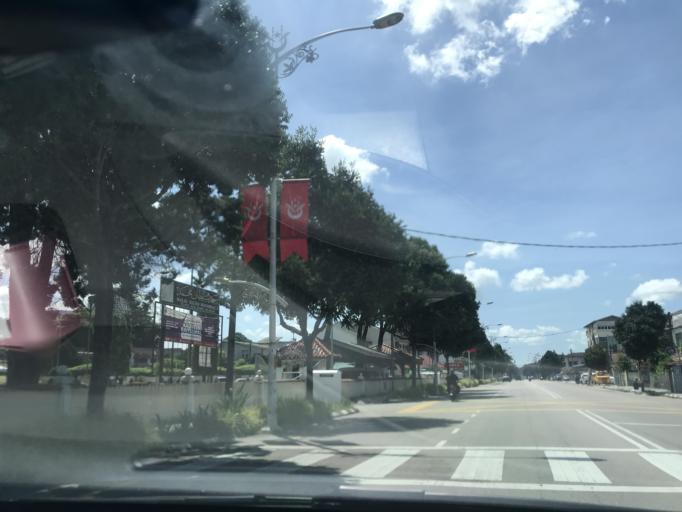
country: MY
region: Kelantan
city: Kota Bharu
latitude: 6.1090
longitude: 102.2438
